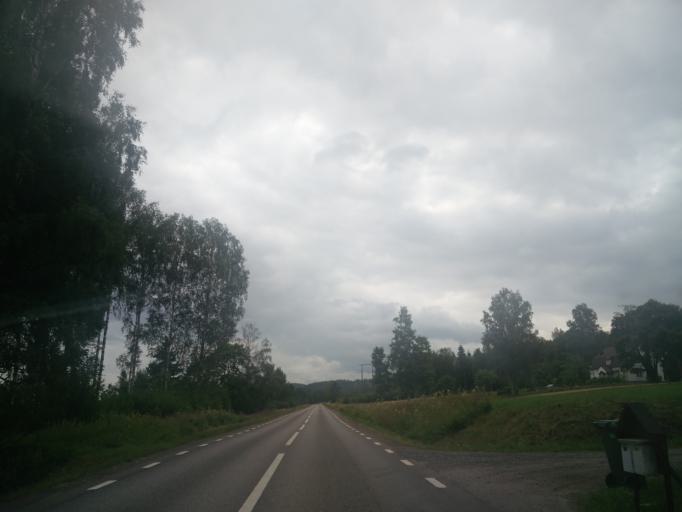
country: SE
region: Vaermland
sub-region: Torsby Kommun
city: Torsby
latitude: 59.9336
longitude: 12.8998
